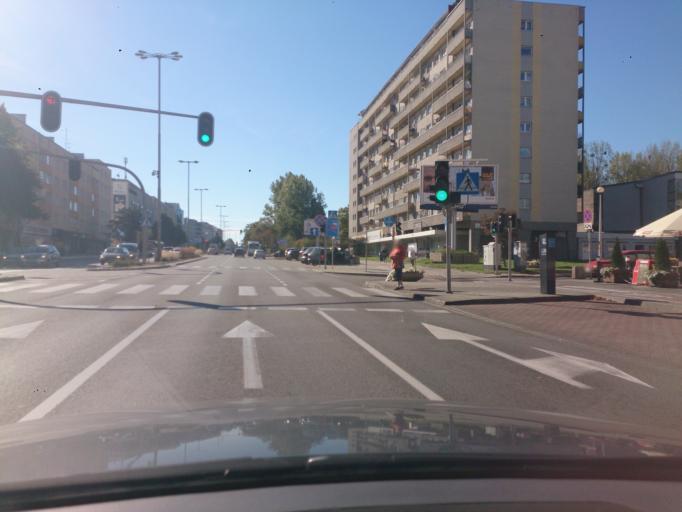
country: PL
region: Pomeranian Voivodeship
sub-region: Gdynia
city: Gdynia
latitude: 54.5154
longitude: 18.5382
